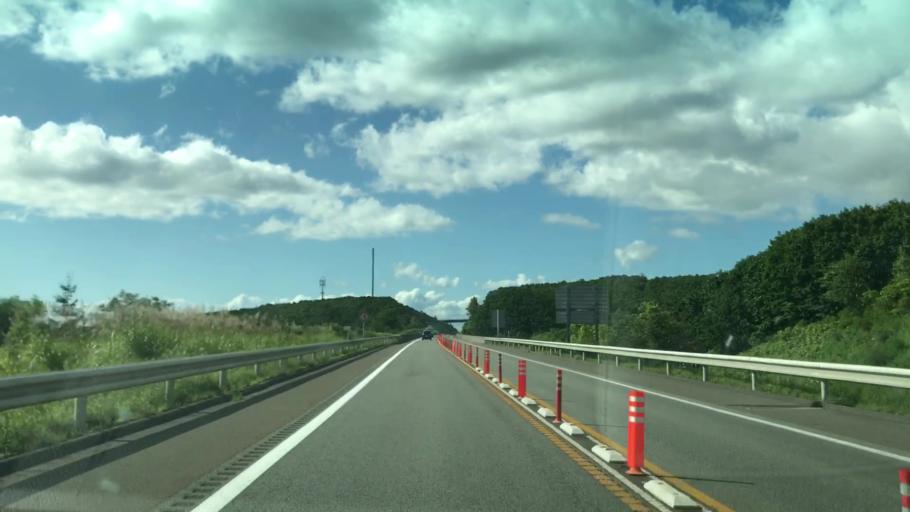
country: JP
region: Hokkaido
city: Muroran
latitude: 42.3923
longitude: 140.9584
